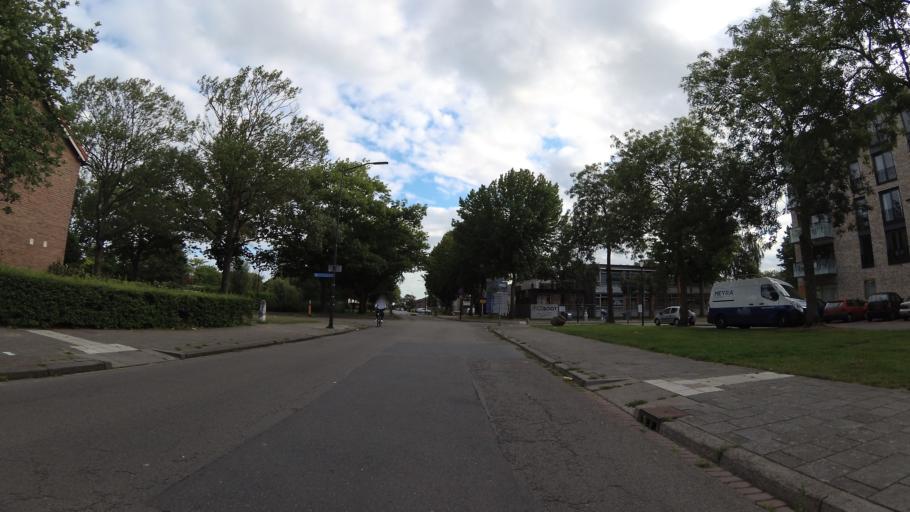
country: NL
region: North Brabant
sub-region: Gemeente Breda
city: Hoge Vucht
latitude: 51.6125
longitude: 4.7802
